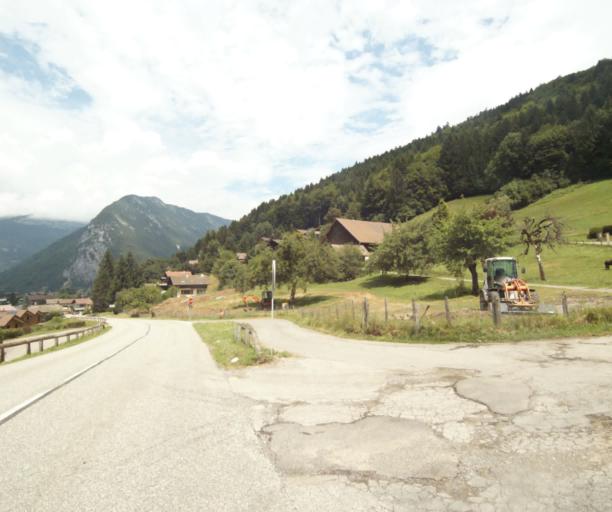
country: FR
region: Rhone-Alpes
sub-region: Departement de la Haute-Savoie
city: Thones
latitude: 45.8669
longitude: 6.3254
